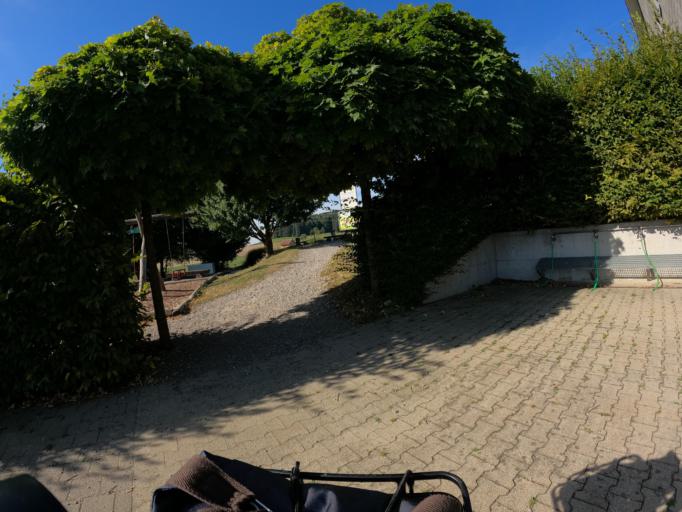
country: CH
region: Zurich
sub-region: Bezirk Dietikon
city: Birmensdorf
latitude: 47.3353
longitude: 8.4330
